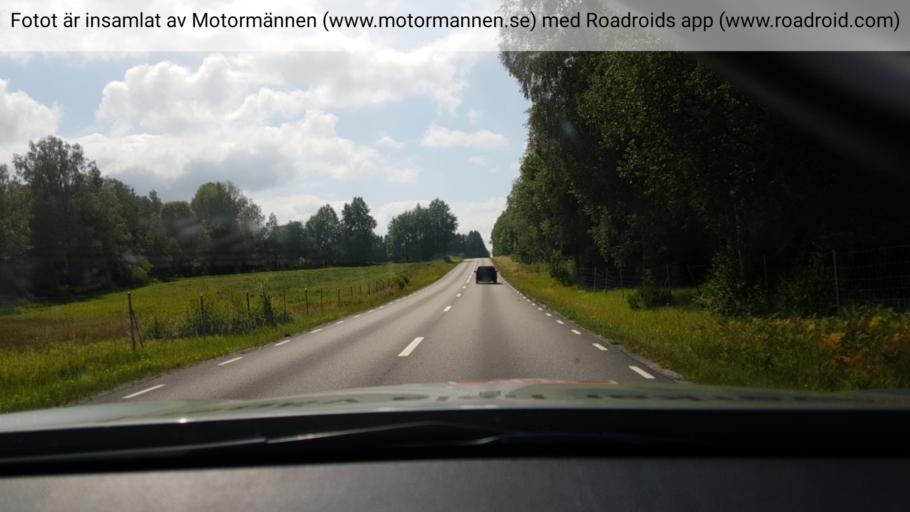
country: SE
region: Vaestra Goetaland
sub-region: Marks Kommun
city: Kinna
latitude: 57.4722
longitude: 12.7640
